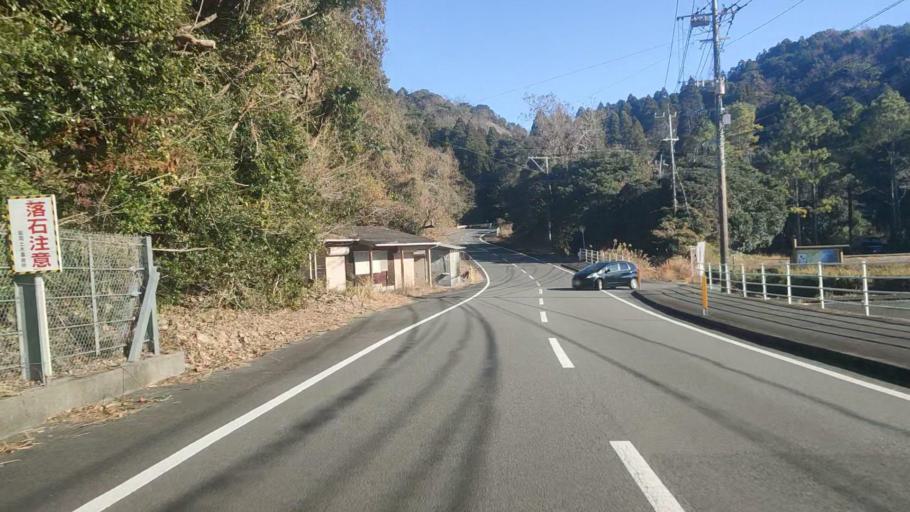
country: JP
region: Miyazaki
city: Nobeoka
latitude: 32.6856
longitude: 131.8032
